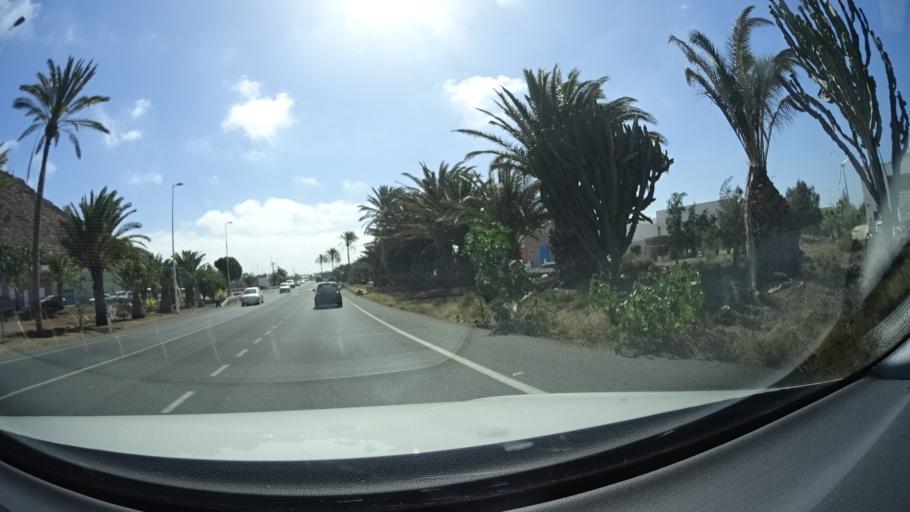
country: ES
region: Canary Islands
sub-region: Provincia de Las Palmas
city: Cruce de Arinaga
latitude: 27.8686
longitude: -15.4155
